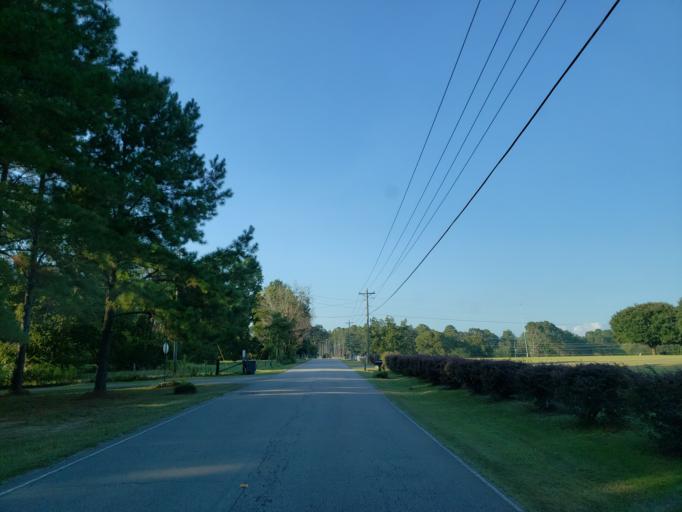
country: US
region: Mississippi
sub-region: Lamar County
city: West Hattiesburg
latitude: 31.3325
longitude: -89.4465
